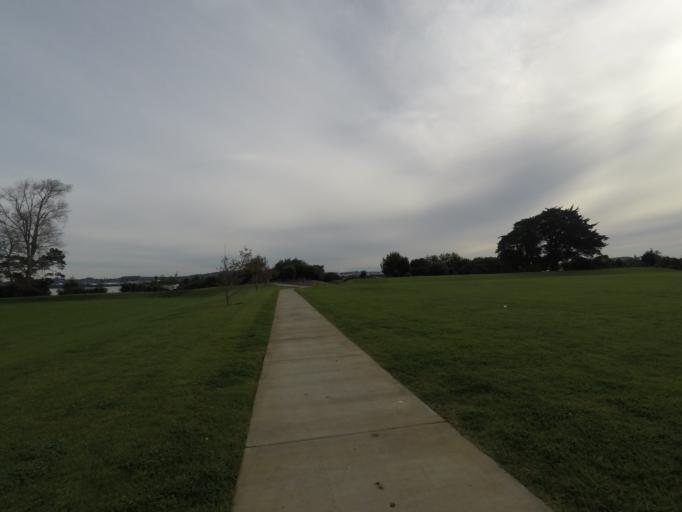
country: NZ
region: Auckland
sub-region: Auckland
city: Mangere
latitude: -36.9452
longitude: 174.8107
